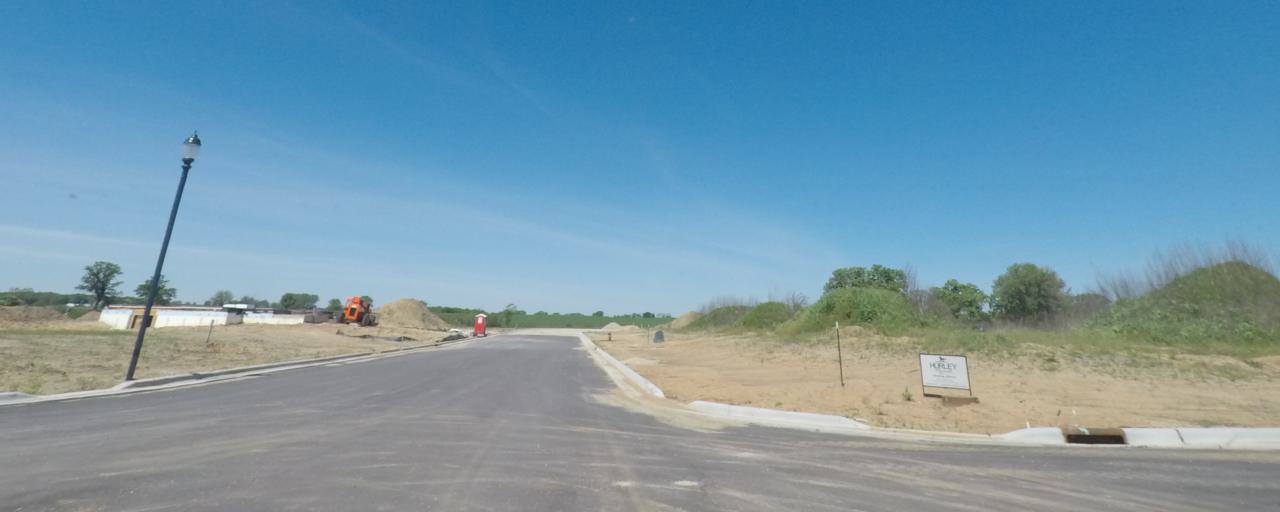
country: US
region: Wisconsin
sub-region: Rock County
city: Evansville
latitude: 42.7744
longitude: -89.3224
